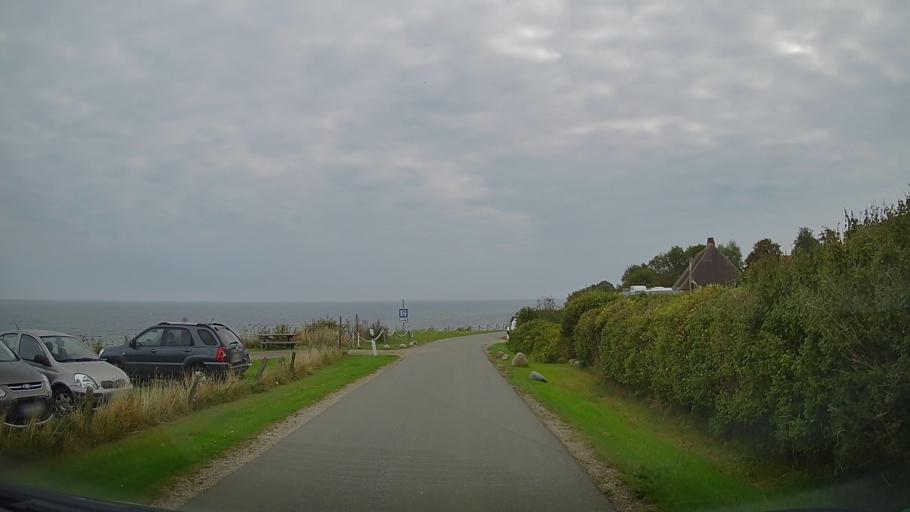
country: DE
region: Schleswig-Holstein
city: Hohenfelde
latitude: 54.3796
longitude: 10.5385
